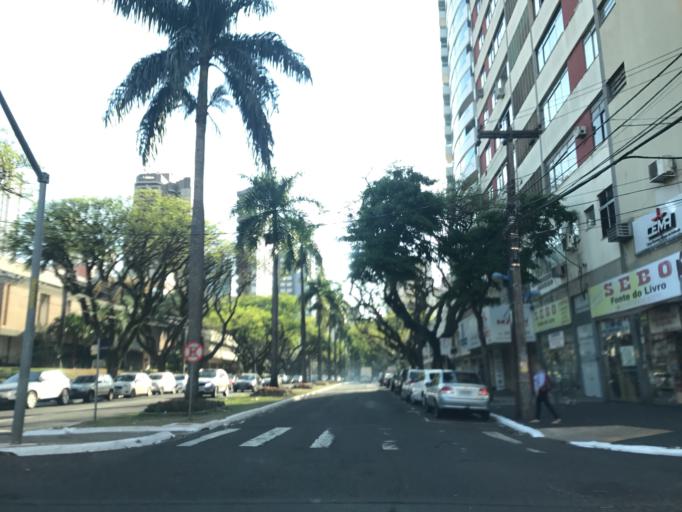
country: BR
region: Parana
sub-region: Maringa
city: Maringa
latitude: -23.4237
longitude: -51.9382
